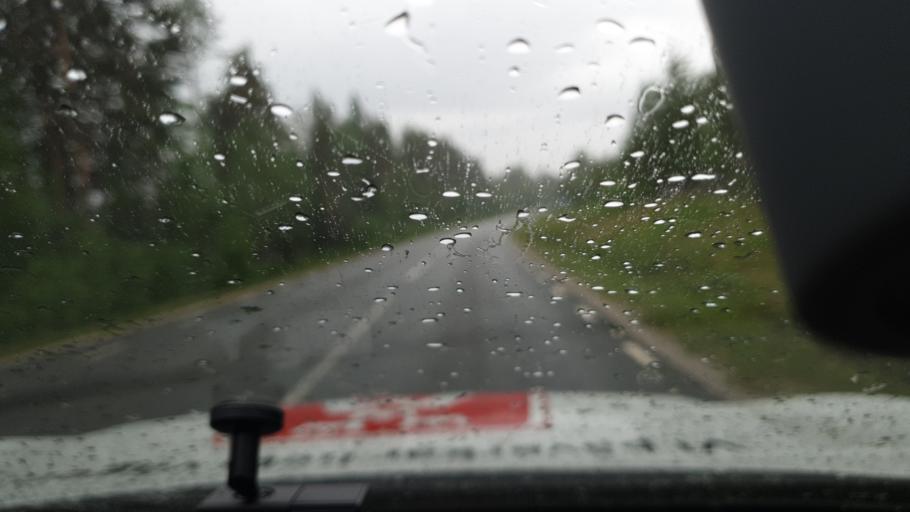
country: SE
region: Vaesterbotten
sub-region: Lycksele Kommun
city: Lycksele
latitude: 64.4423
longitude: 18.9447
